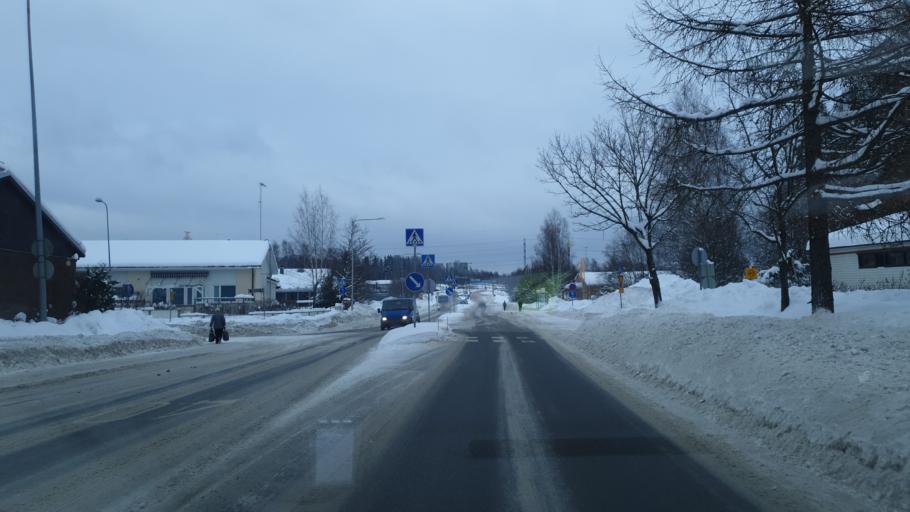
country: FI
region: Uusimaa
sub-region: Helsinki
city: Vantaa
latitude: 60.2655
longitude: 25.0973
